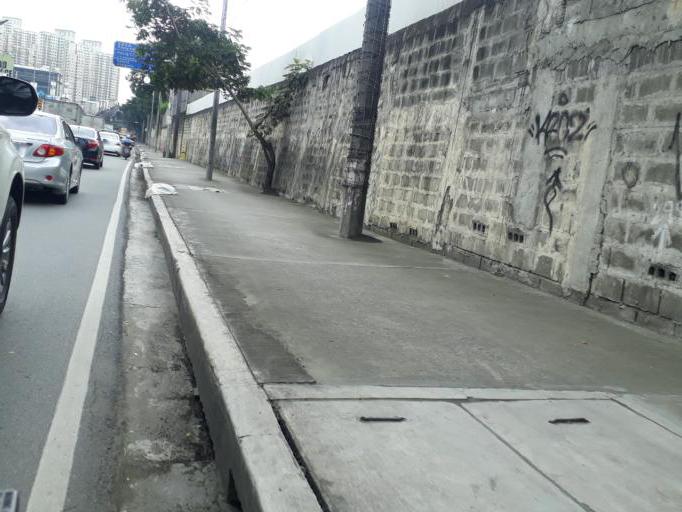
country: PH
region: Metro Manila
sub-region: Pasig
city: Pasig City
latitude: 14.5944
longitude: 121.0796
